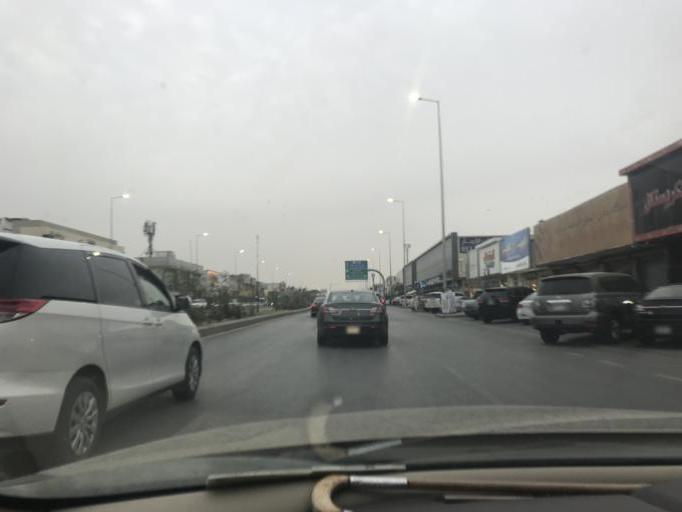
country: SA
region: Ar Riyad
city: Riyadh
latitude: 24.7600
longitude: 46.7650
